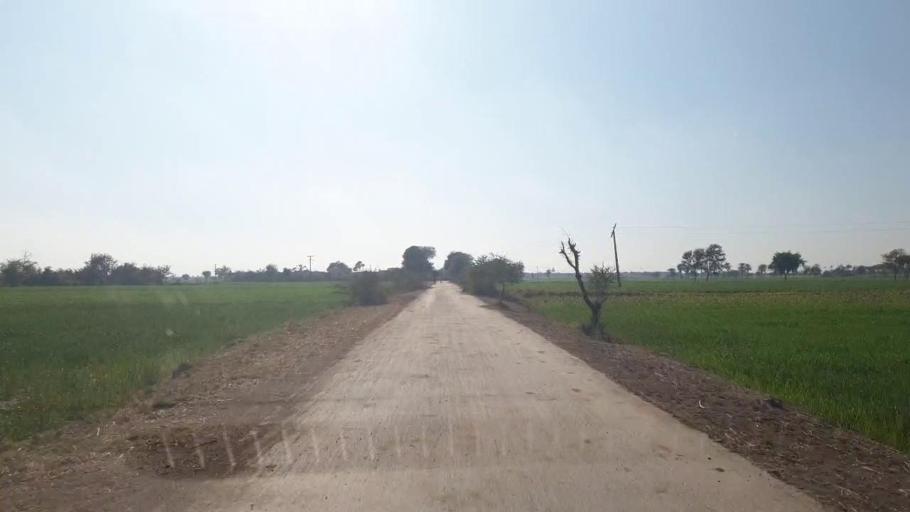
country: PK
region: Sindh
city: Shahdadpur
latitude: 25.9095
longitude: 68.5522
